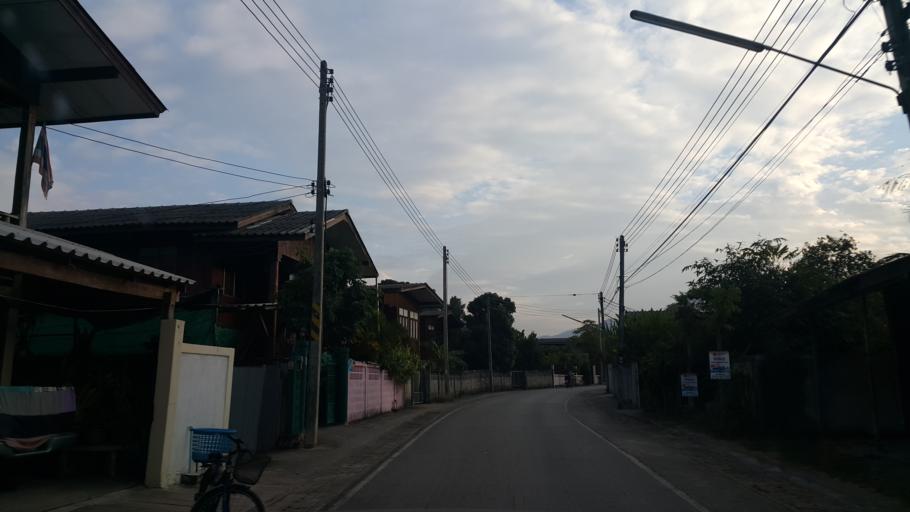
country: TH
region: Lampang
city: Sop Prap
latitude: 17.8685
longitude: 99.3310
